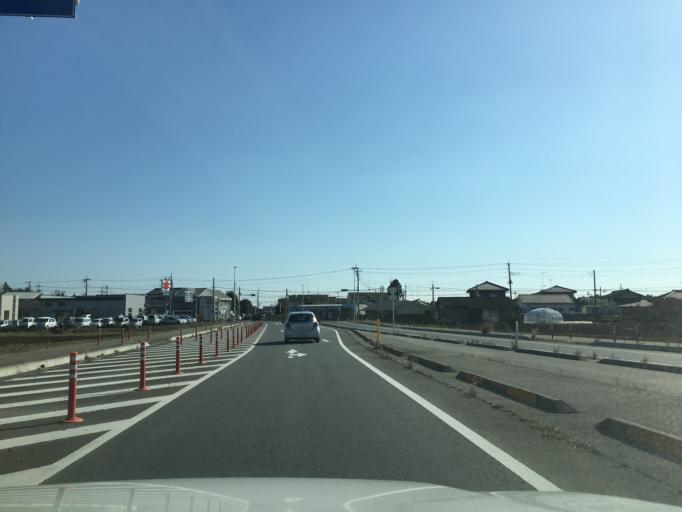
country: JP
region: Ibaraki
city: Omiya
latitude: 36.4785
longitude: 140.3810
